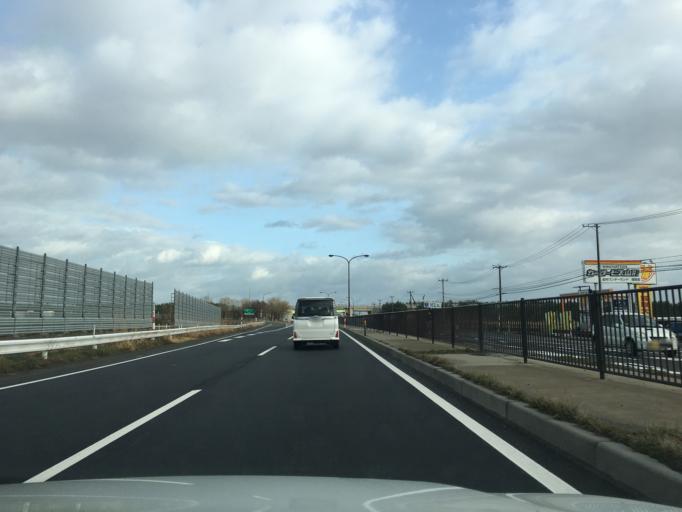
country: JP
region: Yamagata
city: Sakata
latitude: 38.8663
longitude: 139.8428
